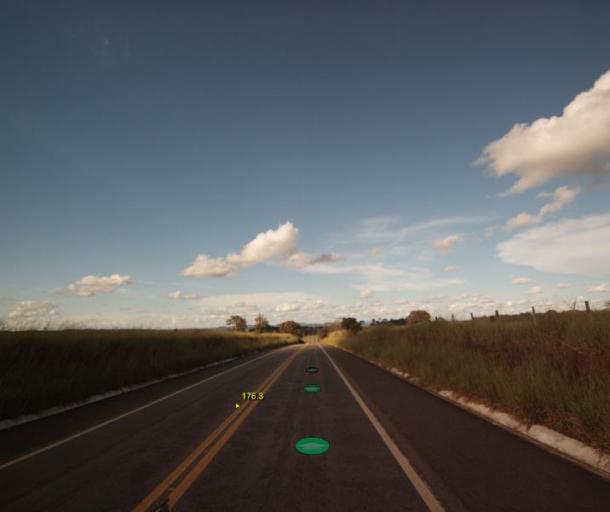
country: BR
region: Goias
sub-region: Itaberai
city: Itaberai
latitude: -15.9732
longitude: -49.6761
